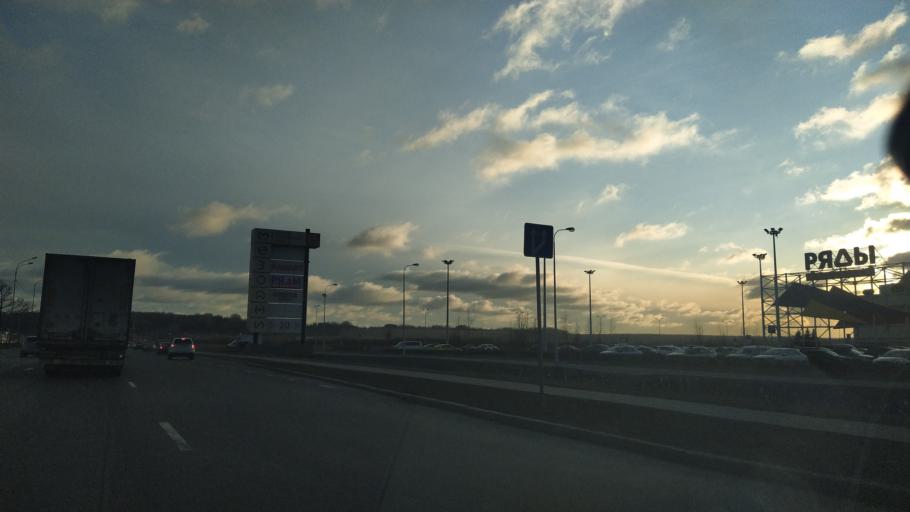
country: RU
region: St.-Petersburg
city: Aleksandrovskaya
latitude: 59.7888
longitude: 30.3246
